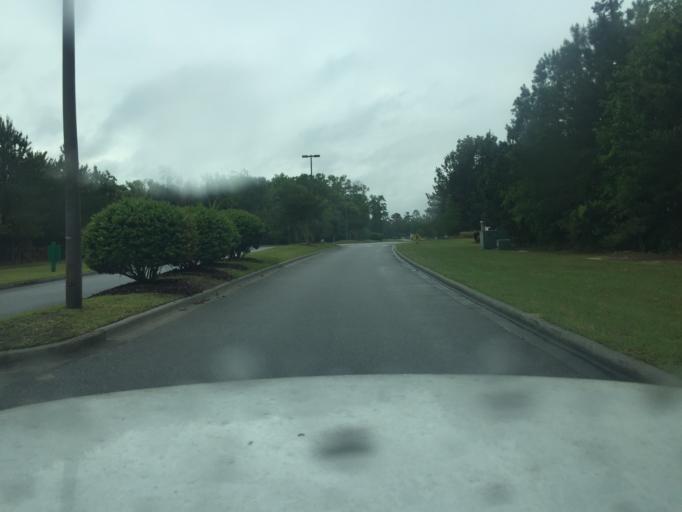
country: US
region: Georgia
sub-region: Chatham County
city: Georgetown
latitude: 32.0463
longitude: -81.2367
